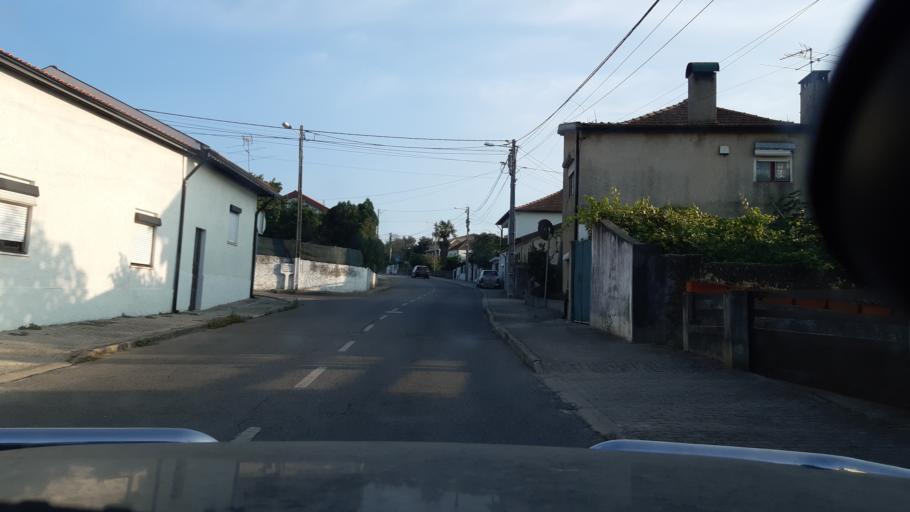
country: PT
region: Aveiro
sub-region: Agueda
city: Agueda
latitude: 40.5549
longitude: -8.4335
